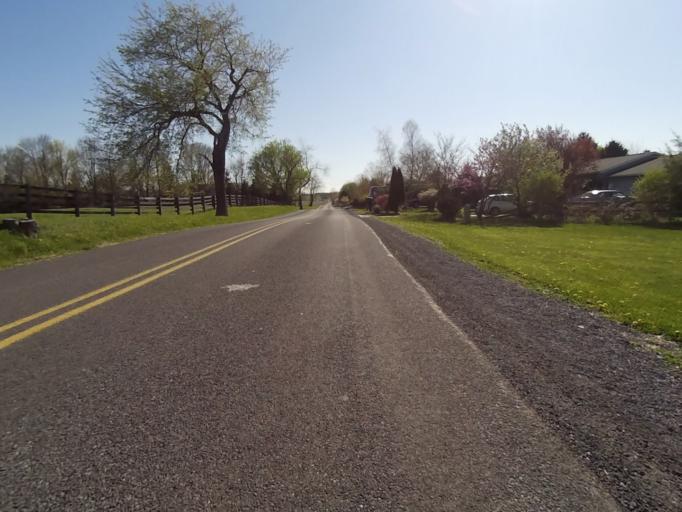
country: US
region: Pennsylvania
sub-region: Centre County
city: Bellefonte
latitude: 40.8828
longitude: -77.8182
